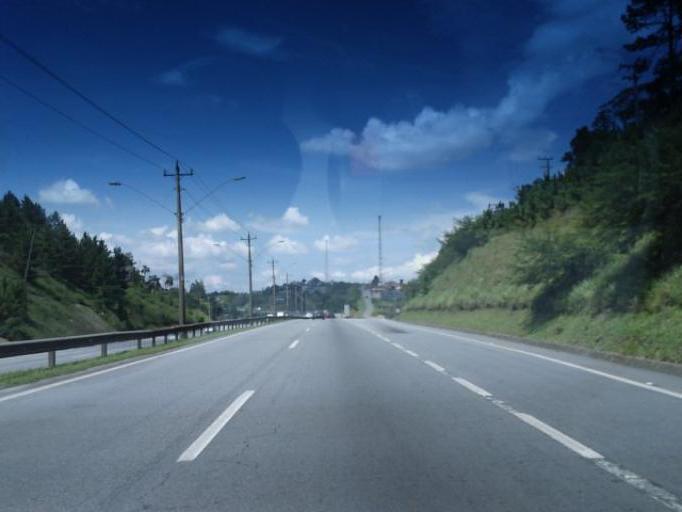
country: BR
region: Sao Paulo
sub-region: Sao Lourenco Da Serra
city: Sao Lourenco da Serra
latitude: -23.8564
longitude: -46.9415
